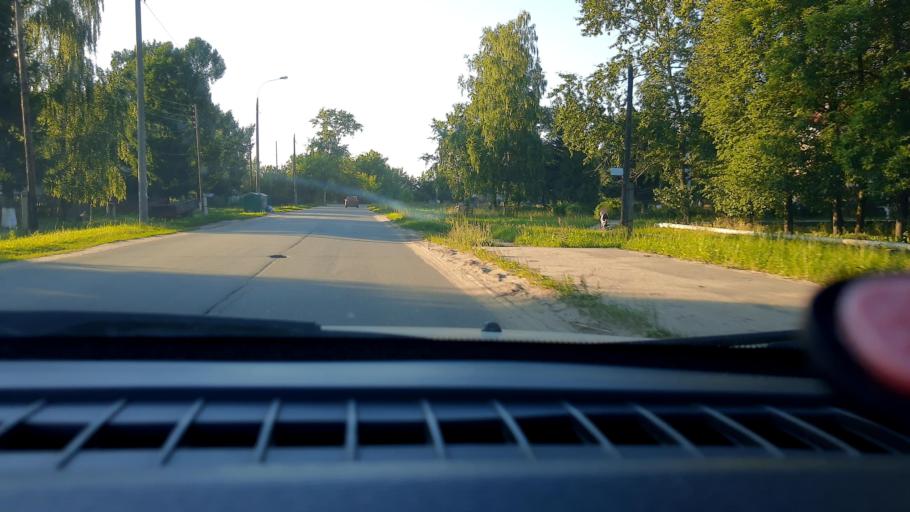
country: RU
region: Nizjnij Novgorod
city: Gorbatovka
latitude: 56.2473
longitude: 43.7479
